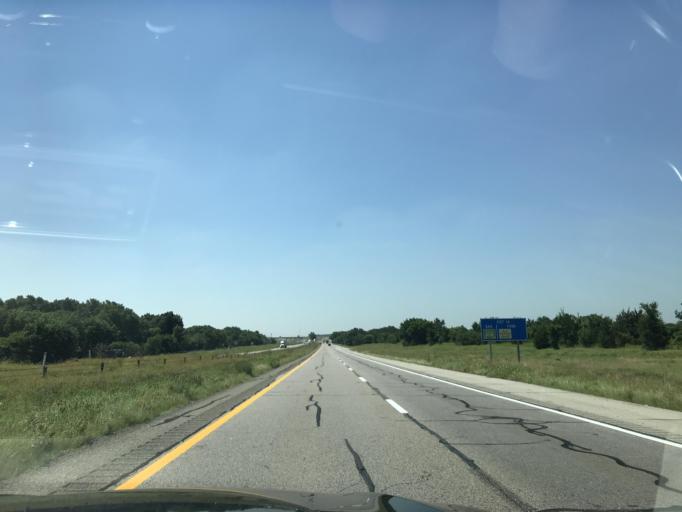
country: US
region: Texas
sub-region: Johnson County
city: Grandview
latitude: 32.2980
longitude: -97.1806
